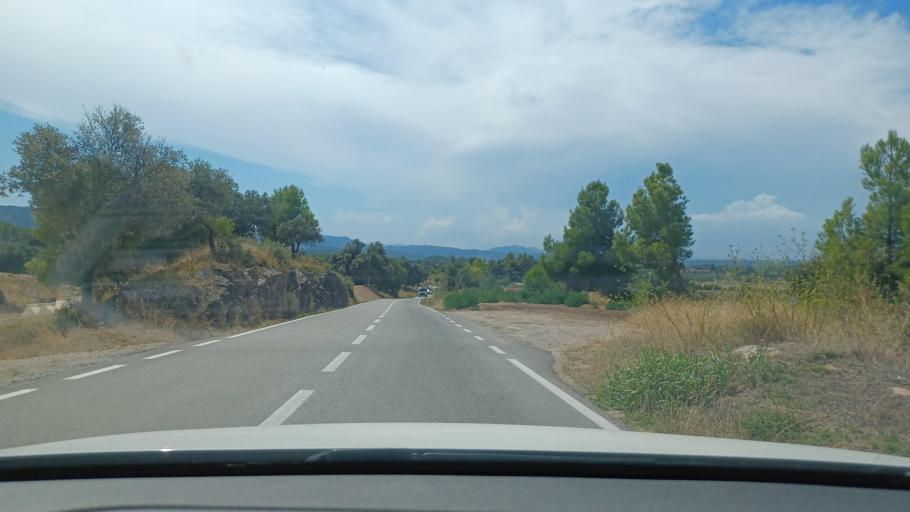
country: ES
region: Catalonia
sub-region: Provincia de Tarragona
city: Horta de Sant Joan
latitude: 40.9483
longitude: 0.3198
